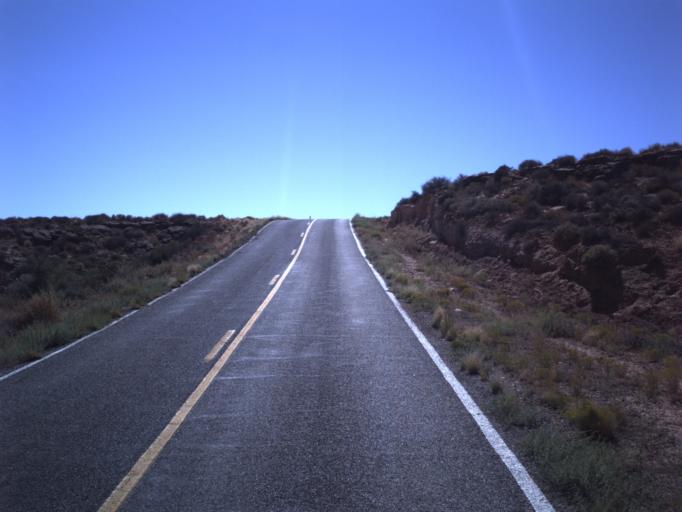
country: US
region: Arizona
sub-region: Navajo County
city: Kayenta
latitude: 37.1835
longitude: -109.9209
